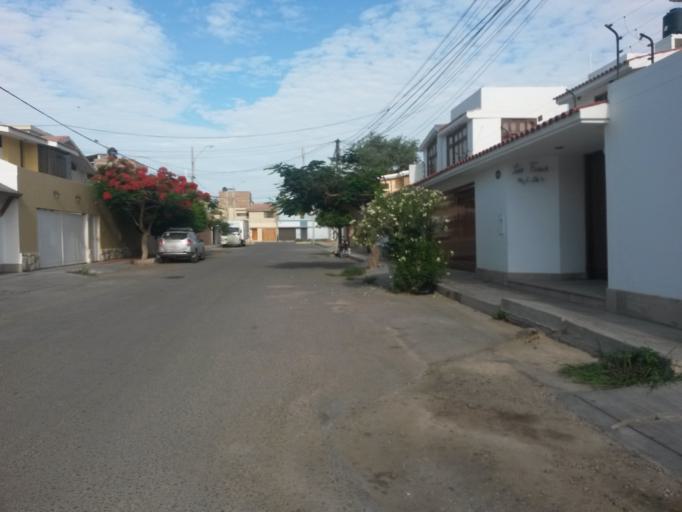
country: PE
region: Piura
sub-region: Provincia de Piura
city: Piura
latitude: -5.1725
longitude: -80.6297
